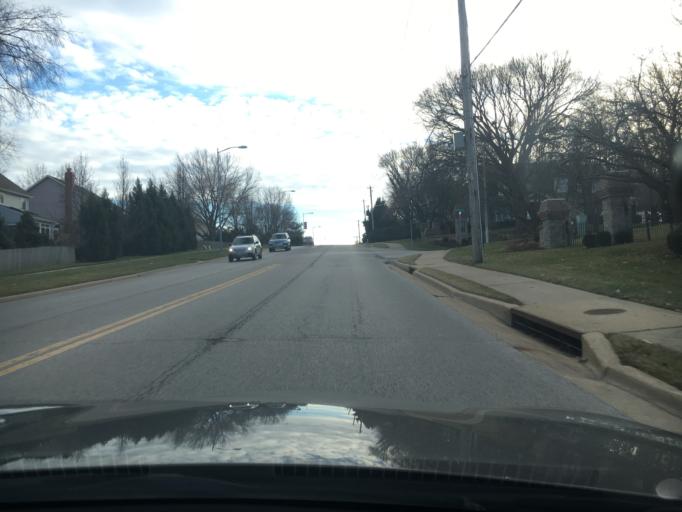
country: US
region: Kansas
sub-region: Johnson County
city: Leawood
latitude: 38.9012
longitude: -94.6306
